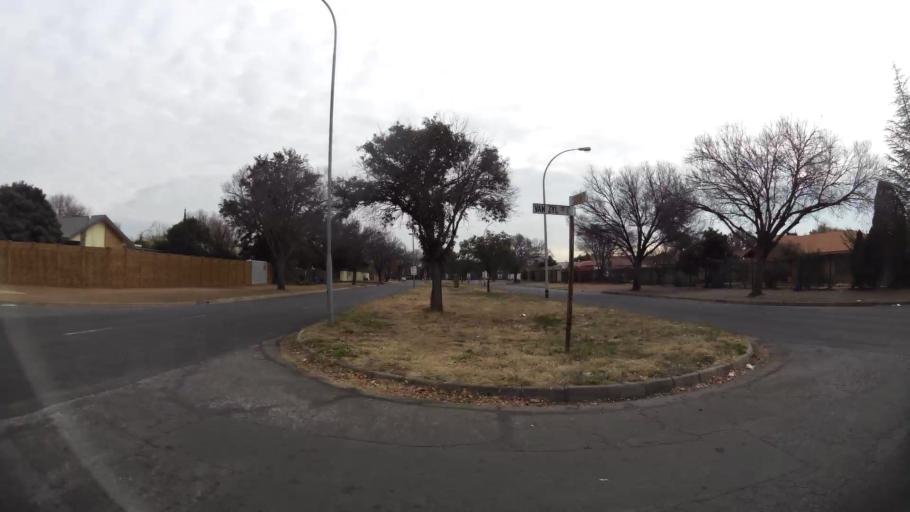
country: ZA
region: Orange Free State
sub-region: Mangaung Metropolitan Municipality
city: Bloemfontein
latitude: -29.1254
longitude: 26.1776
